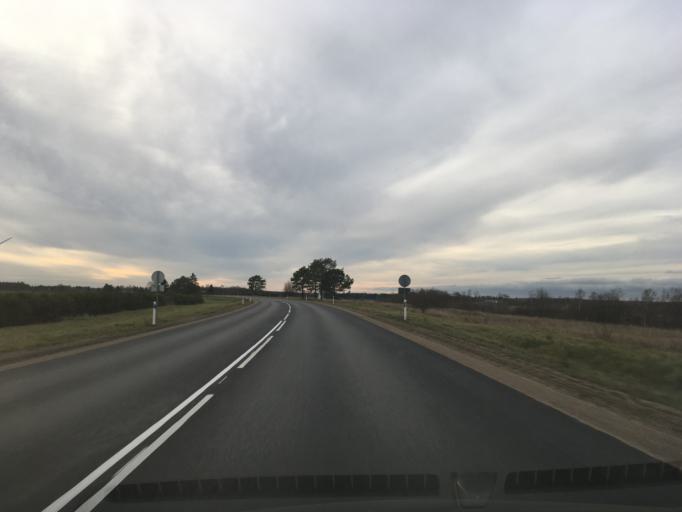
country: EE
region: Ida-Virumaa
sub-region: Aseri vald
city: Aseri
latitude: 59.4453
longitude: 26.7623
